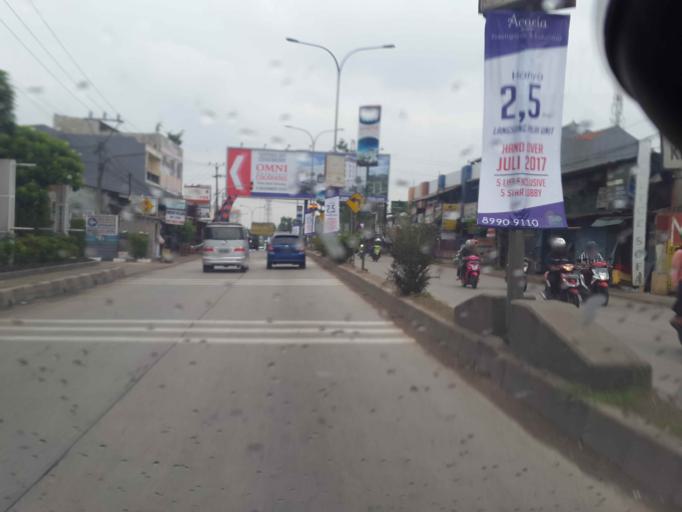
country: ID
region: West Java
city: Cikarang
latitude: -6.3232
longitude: 107.1276
